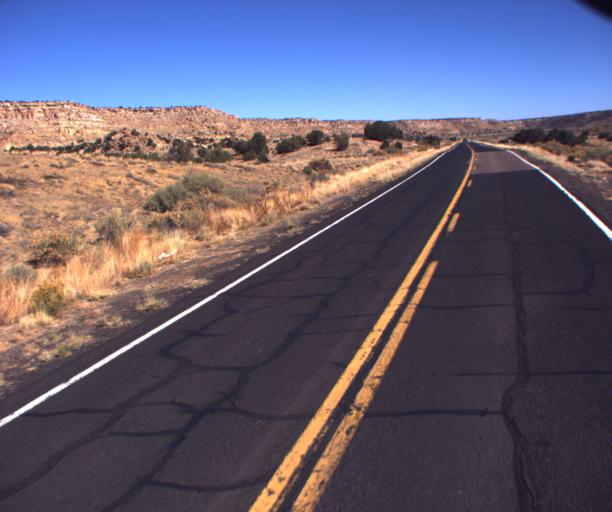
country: US
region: Arizona
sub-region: Navajo County
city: First Mesa
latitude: 35.8313
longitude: -110.2726
